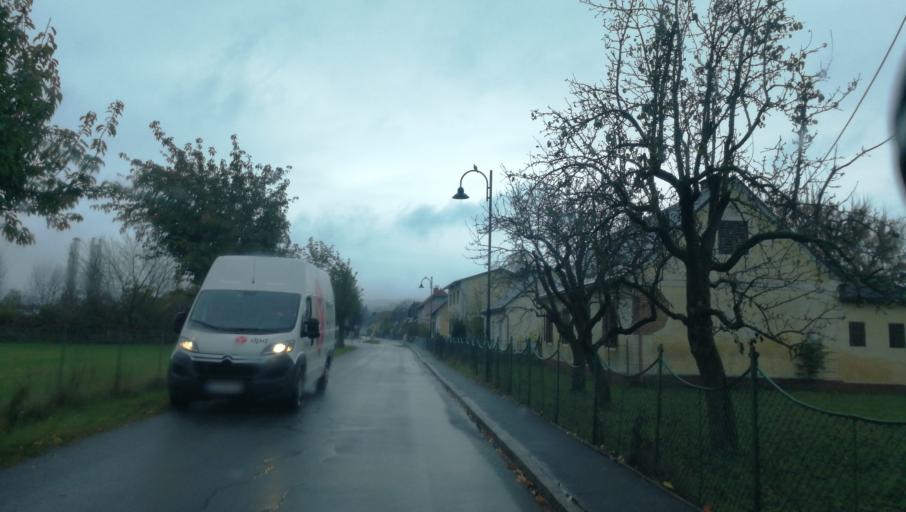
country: AT
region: Styria
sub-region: Politischer Bezirk Leibnitz
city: Strass in Steiermark
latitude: 46.7320
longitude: 15.6223
